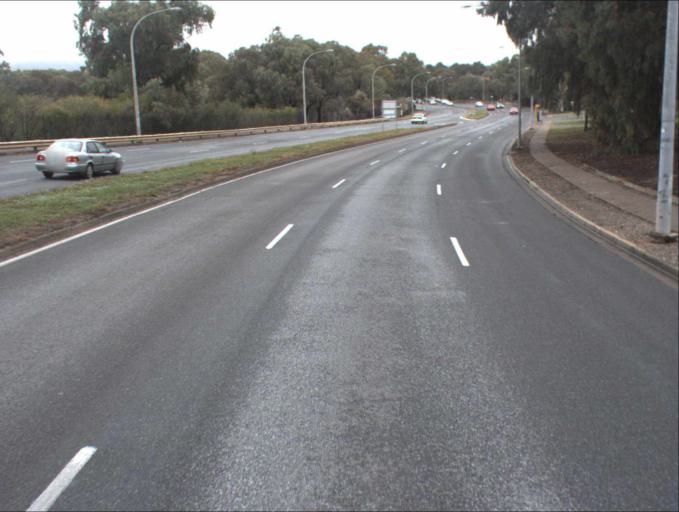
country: AU
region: South Australia
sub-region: Campbelltown
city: Paradise
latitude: -34.8626
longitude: 138.6616
